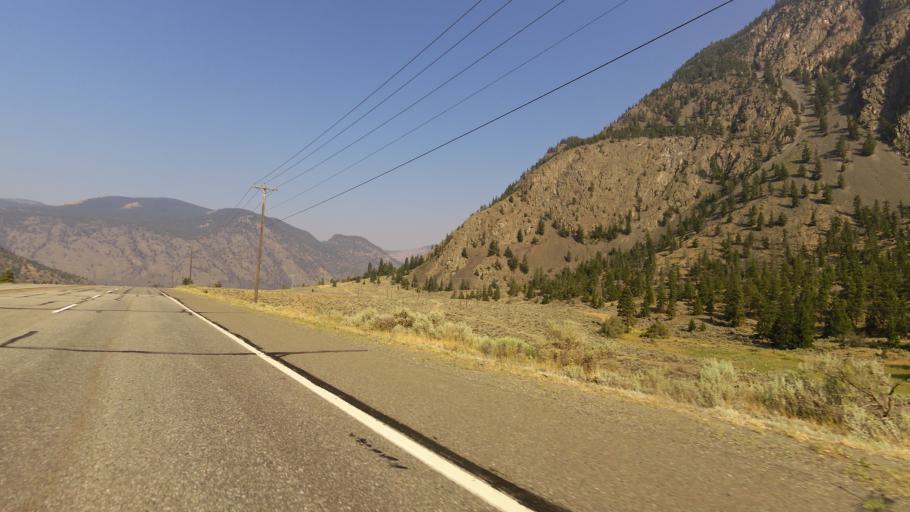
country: CA
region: British Columbia
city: Oliver
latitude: 49.2205
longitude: -119.9438
